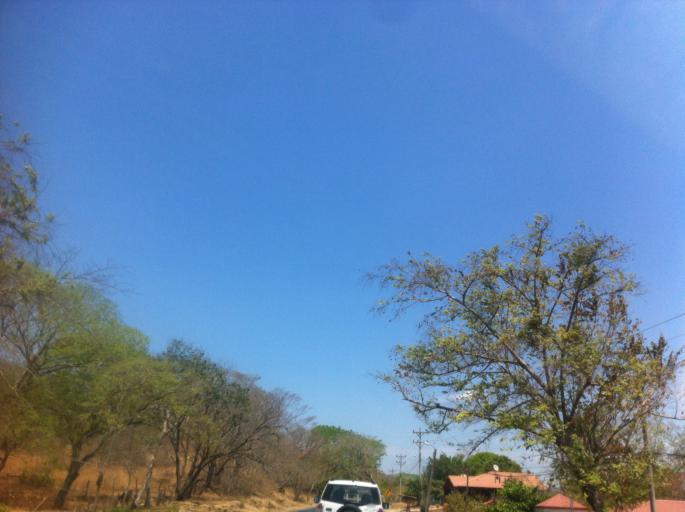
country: CR
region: Guanacaste
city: Belen
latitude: 10.3805
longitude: -85.5804
